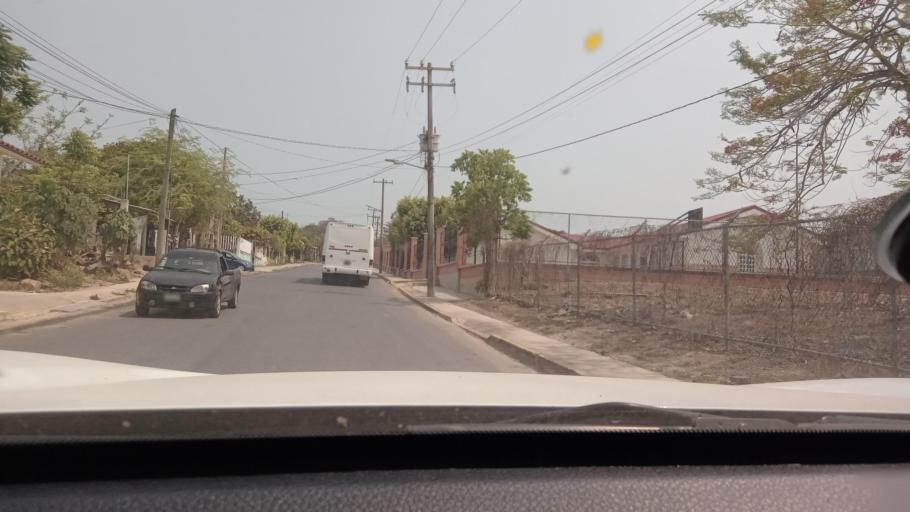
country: MX
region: Veracruz
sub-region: Minatitlan
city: Las Lomas
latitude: 17.9738
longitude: -94.5685
